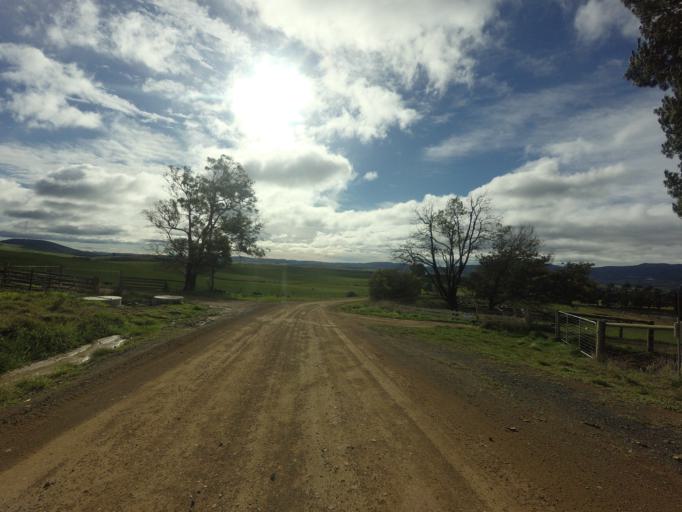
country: AU
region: Tasmania
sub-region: Derwent Valley
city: New Norfolk
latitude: -42.7190
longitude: 146.8743
